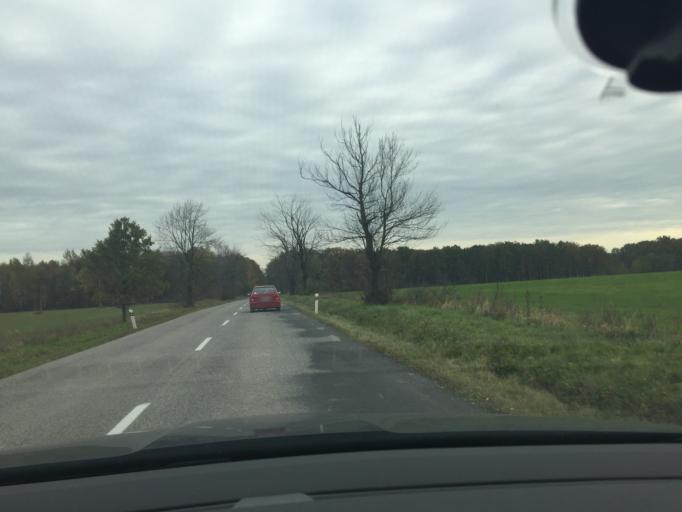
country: SK
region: Presovsky
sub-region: Okres Presov
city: Presov
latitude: 48.9410
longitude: 21.3052
